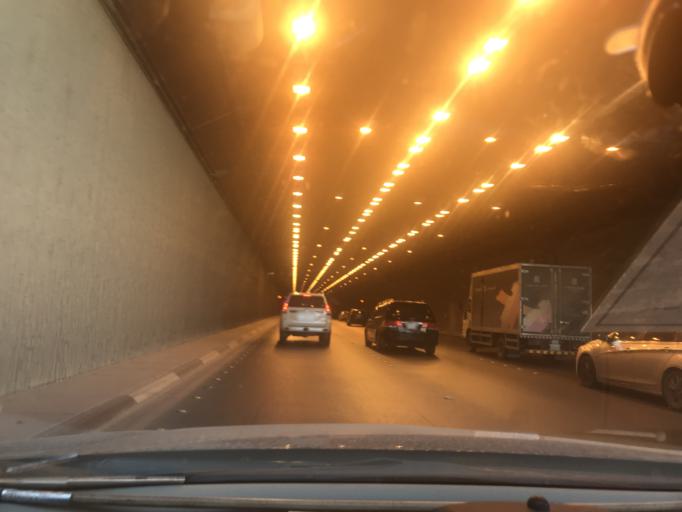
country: SA
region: Ar Riyad
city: Riyadh
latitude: 24.7293
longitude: 46.7180
